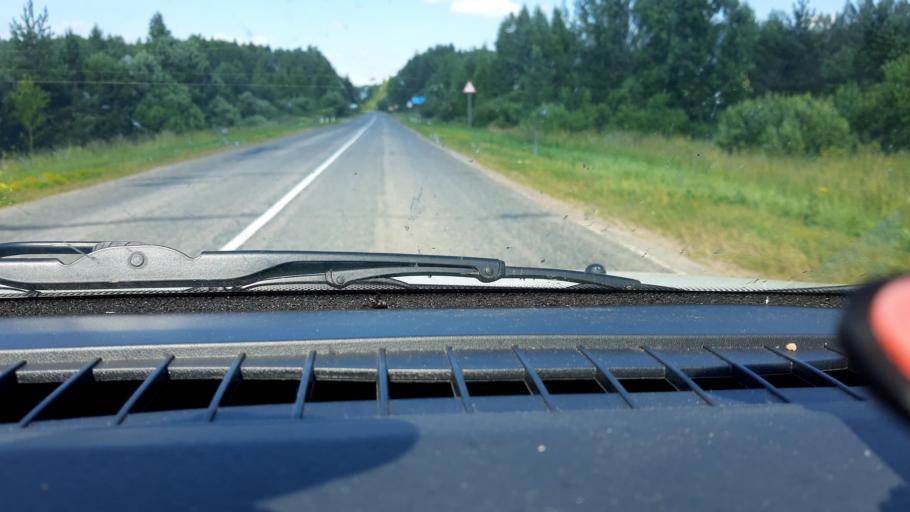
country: RU
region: Nizjnij Novgorod
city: Tonkino
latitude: 57.3229
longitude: 46.4743
